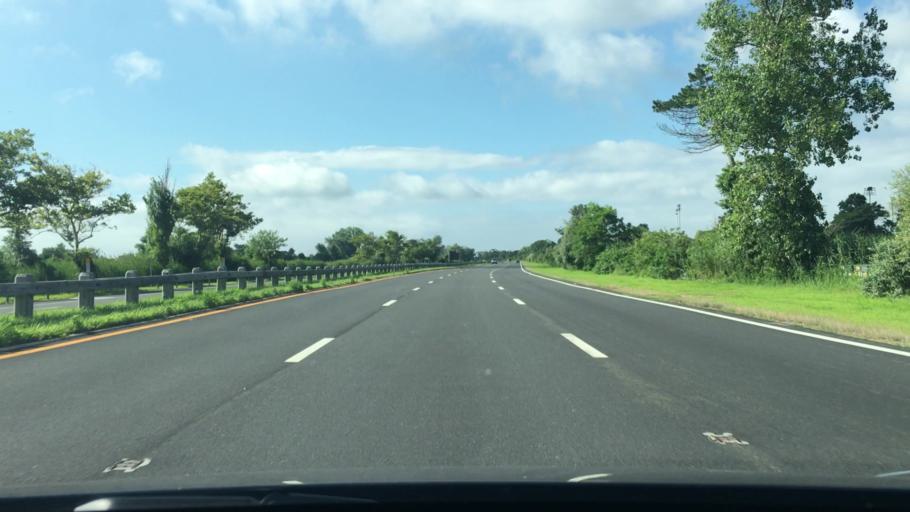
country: US
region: New York
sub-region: Nassau County
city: Bellmore
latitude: 40.6494
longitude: -73.5098
